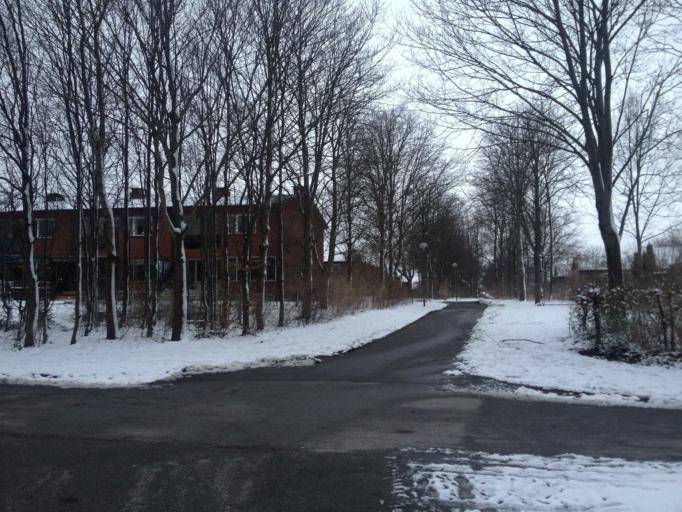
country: SE
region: Skane
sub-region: Lunds Kommun
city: Lund
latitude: 55.7239
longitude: 13.2130
